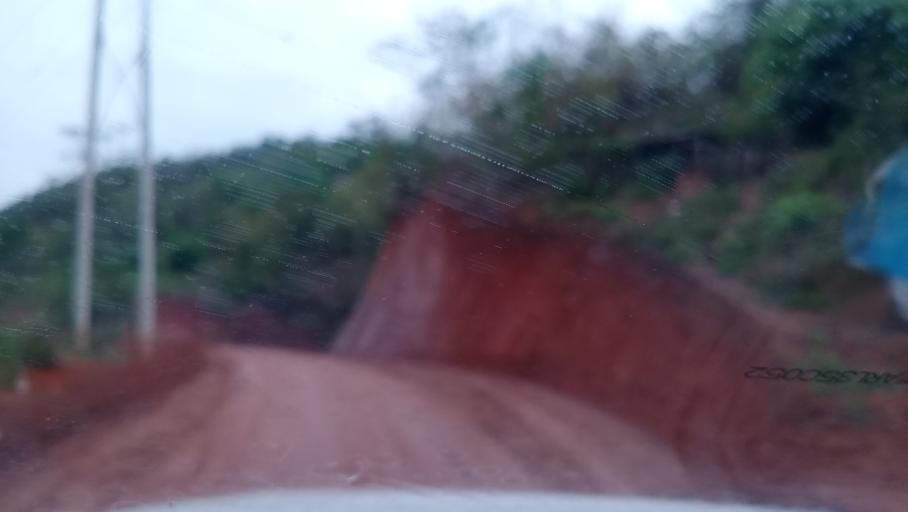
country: CN
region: Yunnan
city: Menglie
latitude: 22.2070
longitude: 101.6649
